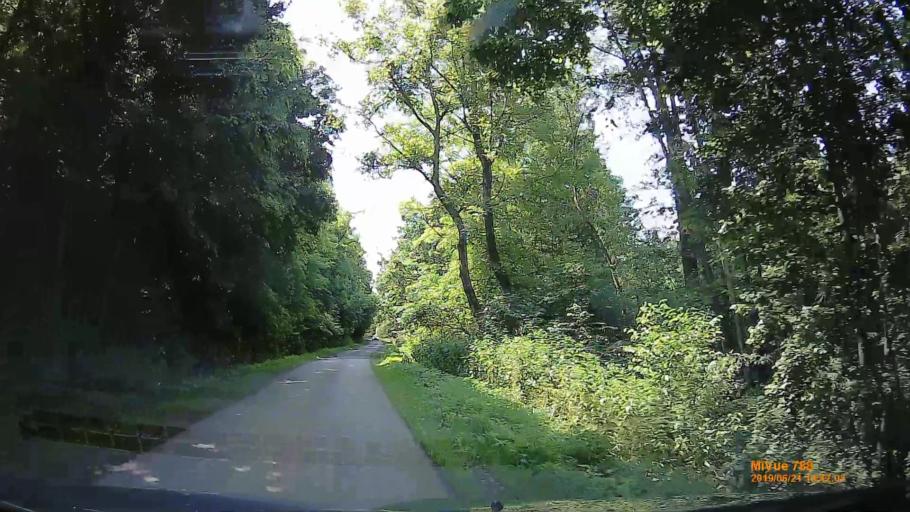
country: HU
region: Baranya
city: Buekkoesd
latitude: 46.1310
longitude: 18.0039
